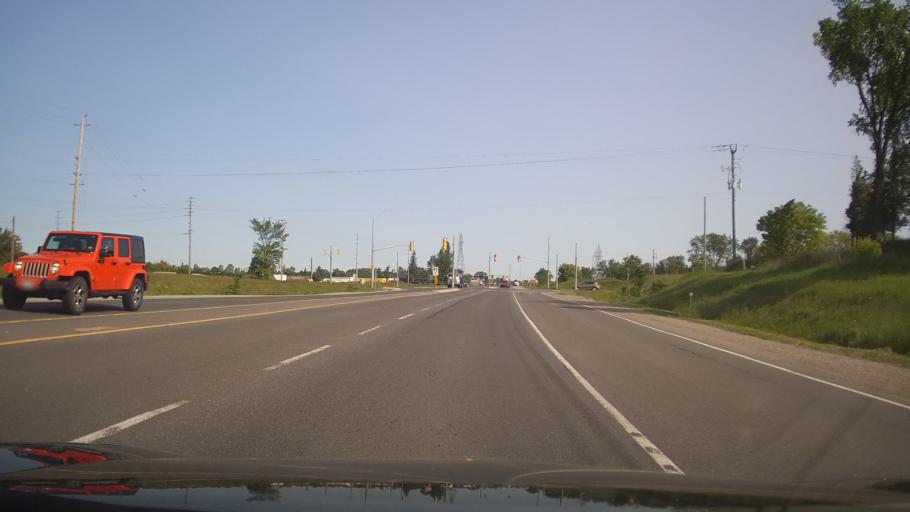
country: CA
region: Ontario
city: Peterborough
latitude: 44.2781
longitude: -78.4185
